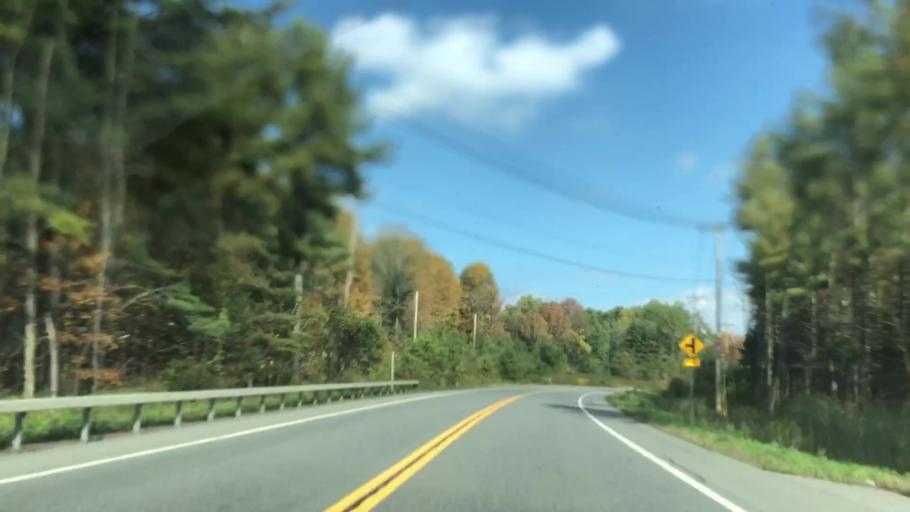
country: US
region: New York
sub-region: Warren County
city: Queensbury
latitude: 43.3944
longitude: -73.6400
